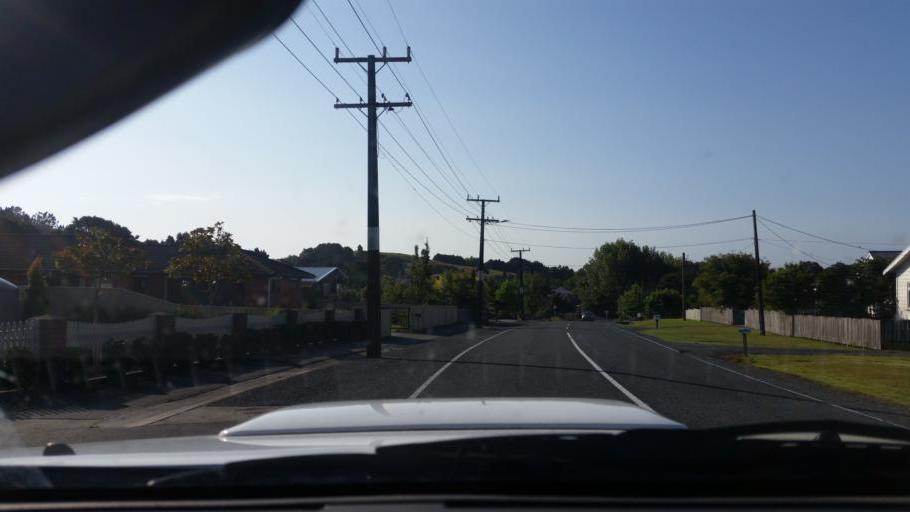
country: NZ
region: Northland
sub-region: Whangarei
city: Ruakaka
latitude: -36.1072
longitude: 174.2285
